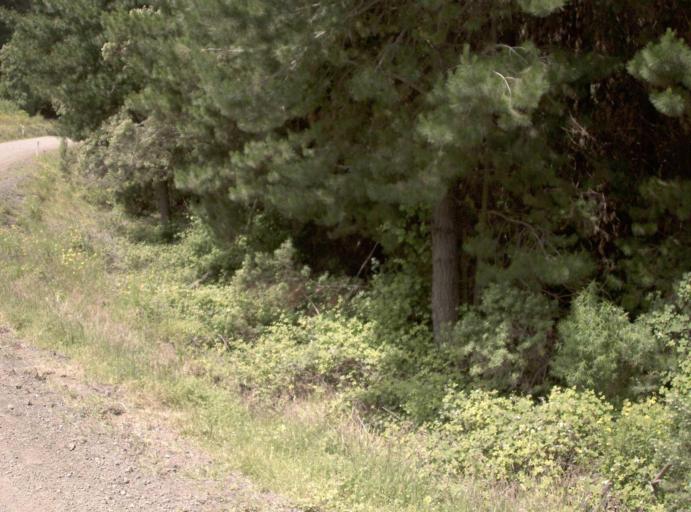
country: AU
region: Victoria
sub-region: Latrobe
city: Traralgon
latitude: -38.3878
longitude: 146.6615
